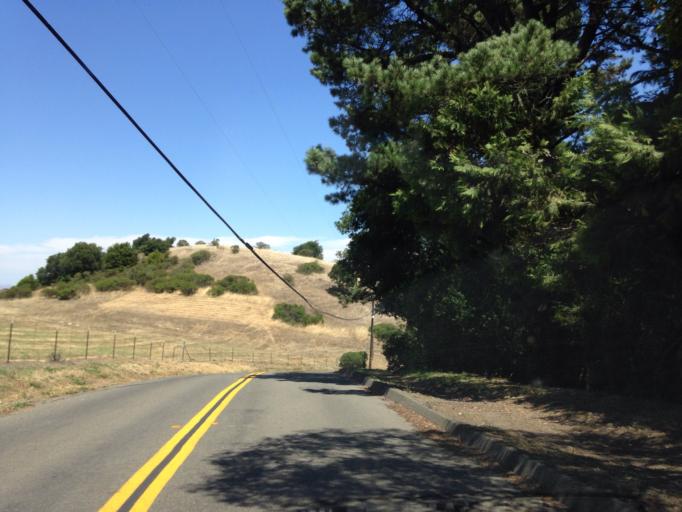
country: US
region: California
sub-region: Contra Costa County
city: Orinda
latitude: 37.8804
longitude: -122.2168
